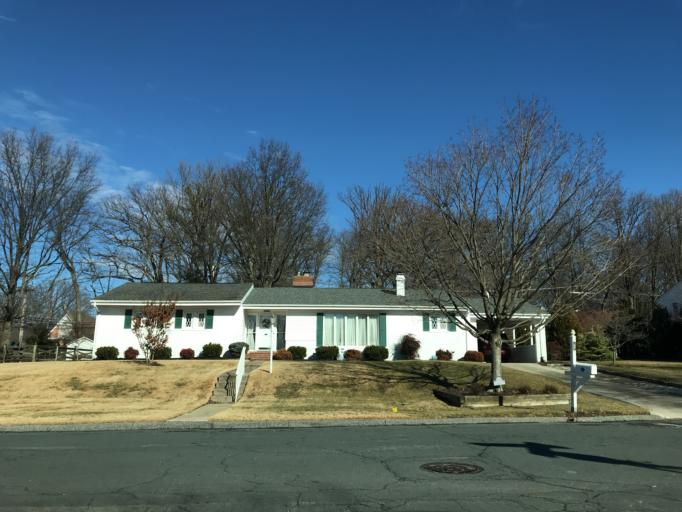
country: US
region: Maryland
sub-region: Baltimore County
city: Hampton
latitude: 39.4121
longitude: -76.5766
